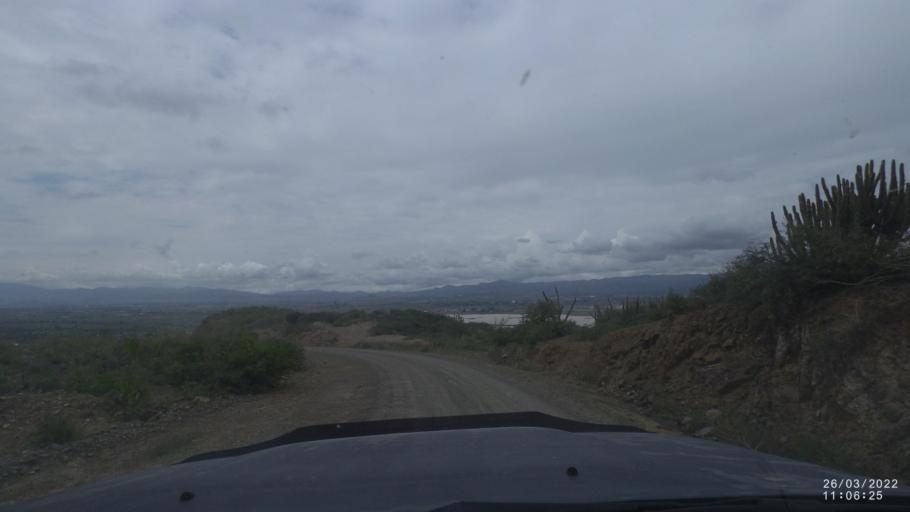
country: BO
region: Cochabamba
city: Tarata
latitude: -17.5330
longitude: -66.0187
